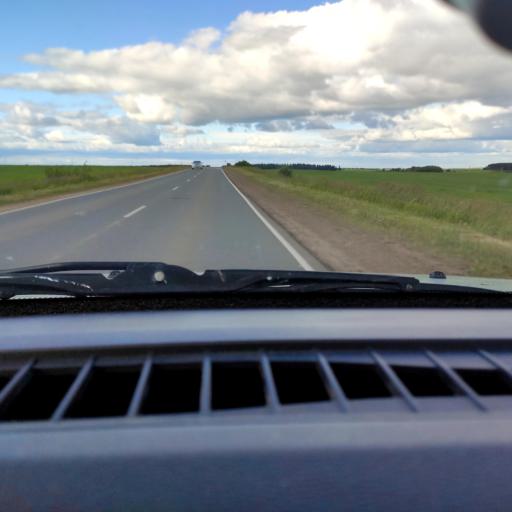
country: RU
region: Perm
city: Kungur
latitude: 57.3831
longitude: 56.8544
